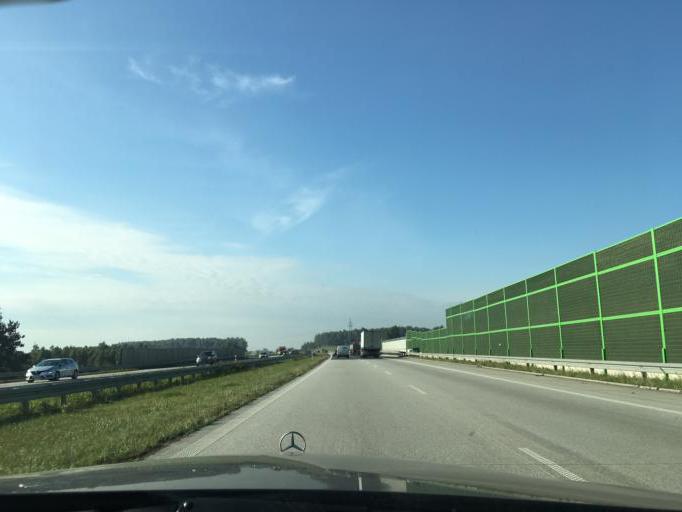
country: PL
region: Lodz Voivodeship
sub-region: Powiat lodzki wschodni
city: Andrespol
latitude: 51.7751
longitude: 19.6033
